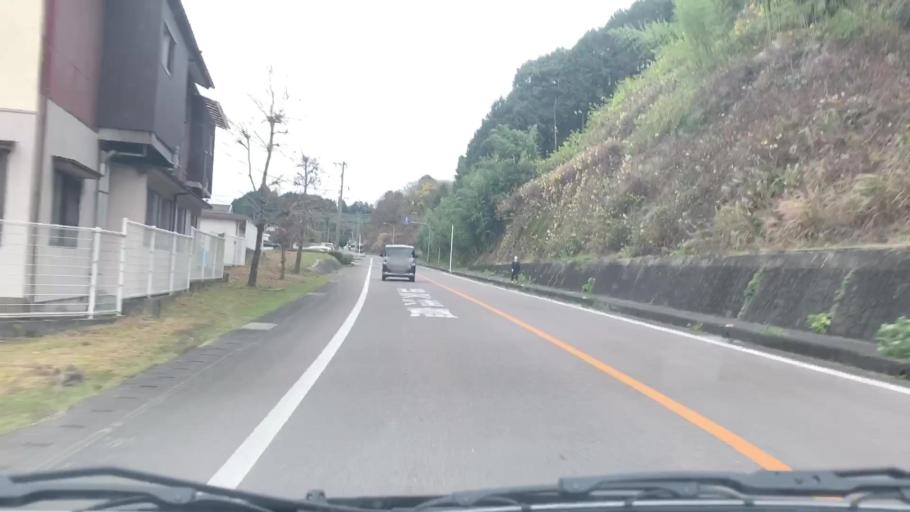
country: JP
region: Saga Prefecture
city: Ureshinomachi-shimojuku
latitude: 33.0991
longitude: 130.0010
